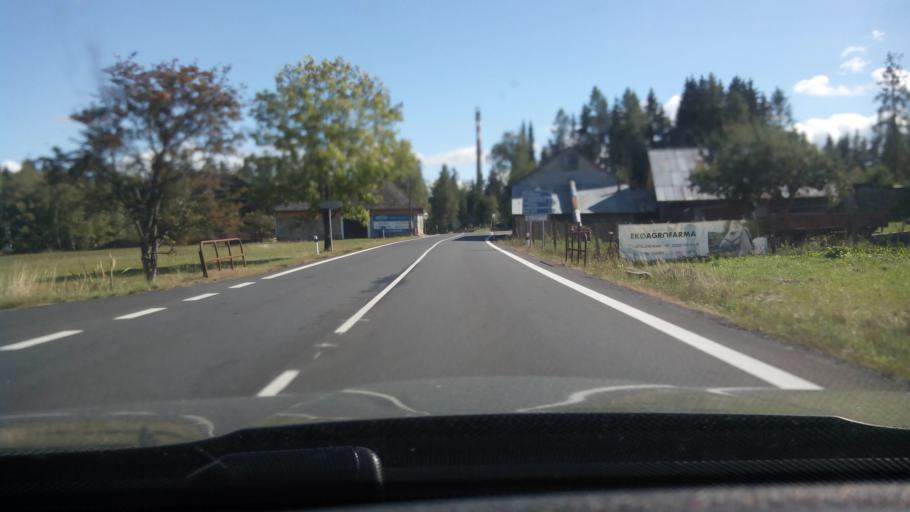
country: CZ
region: Jihocesky
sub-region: Okres Prachatice
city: Zdikov
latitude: 49.0636
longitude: 13.7362
